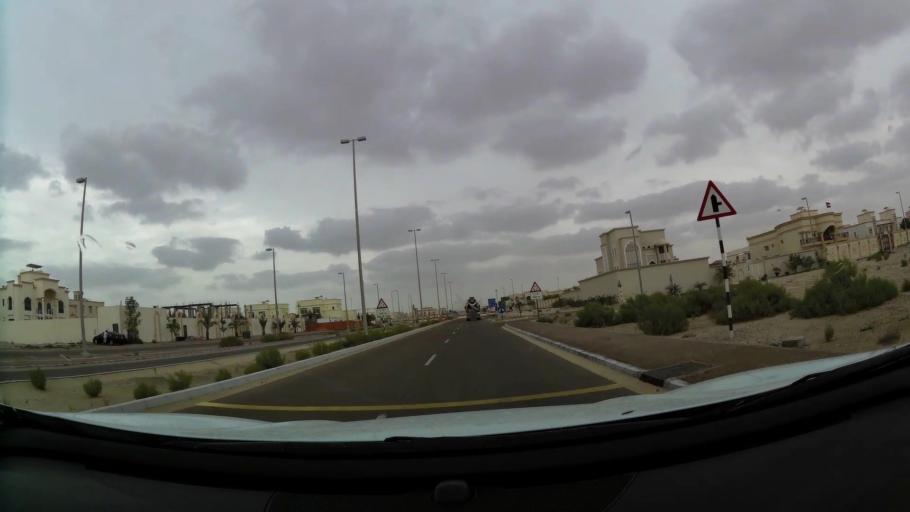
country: AE
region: Abu Dhabi
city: Abu Dhabi
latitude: 24.3748
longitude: 54.6433
